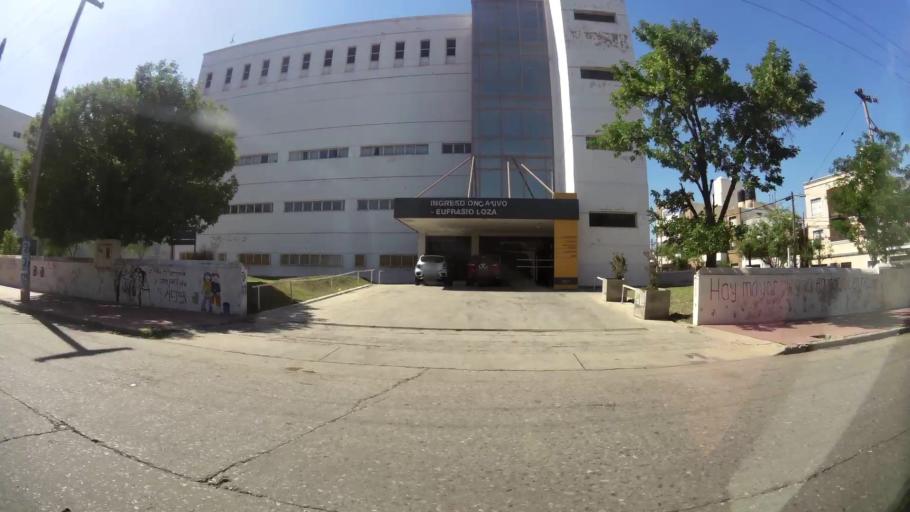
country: AR
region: Cordoba
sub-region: Departamento de Capital
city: Cordoba
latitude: -31.4070
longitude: -64.1573
